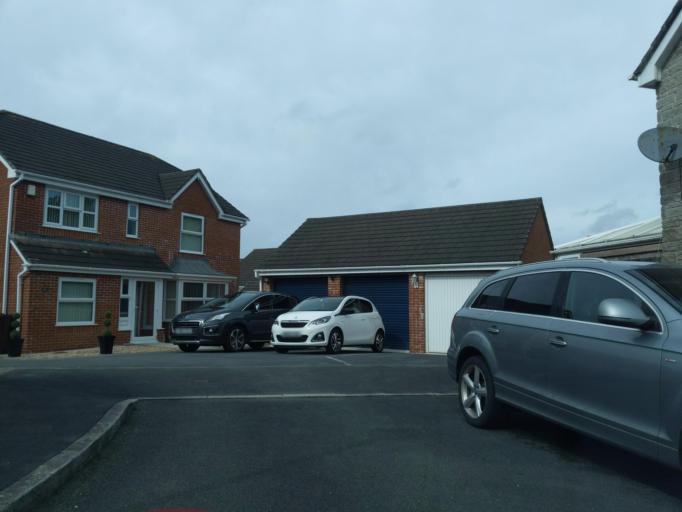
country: GB
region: England
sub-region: Plymouth
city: Plymouth
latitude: 50.4075
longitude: -4.1411
